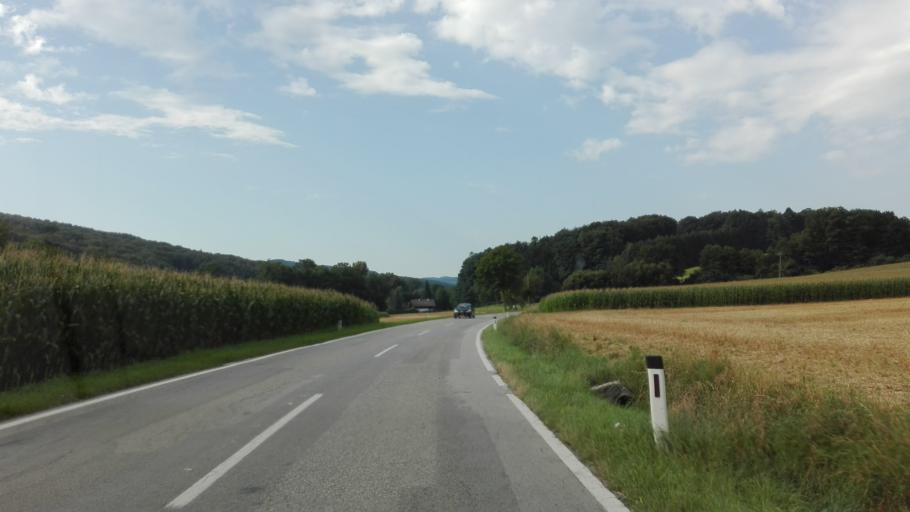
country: AT
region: Lower Austria
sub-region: Politischer Bezirk Sankt Polten
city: Kasten bei Boheimkirchen
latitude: 48.1621
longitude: 15.7577
